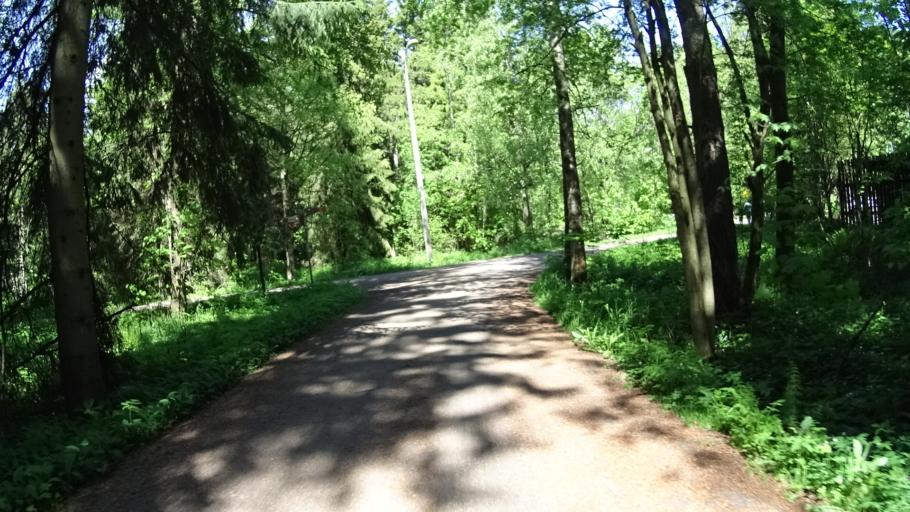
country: FI
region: Uusimaa
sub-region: Helsinki
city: Helsinki
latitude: 60.2279
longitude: 24.9142
